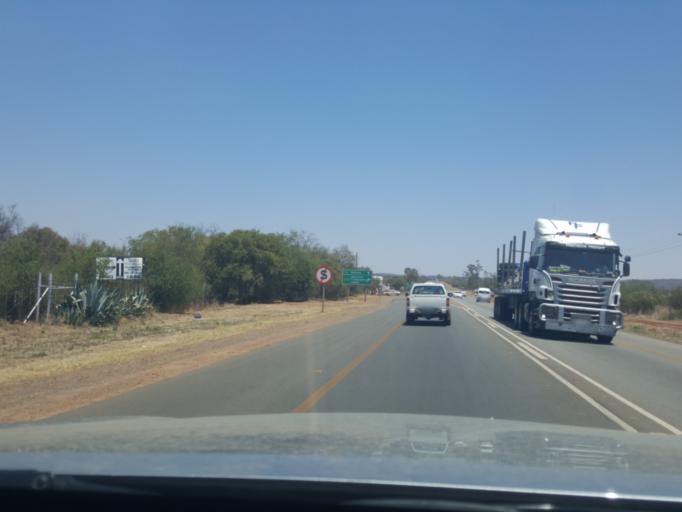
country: ZA
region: North-West
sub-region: Ngaka Modiri Molema District Municipality
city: Zeerust
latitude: -25.5585
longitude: 26.0649
